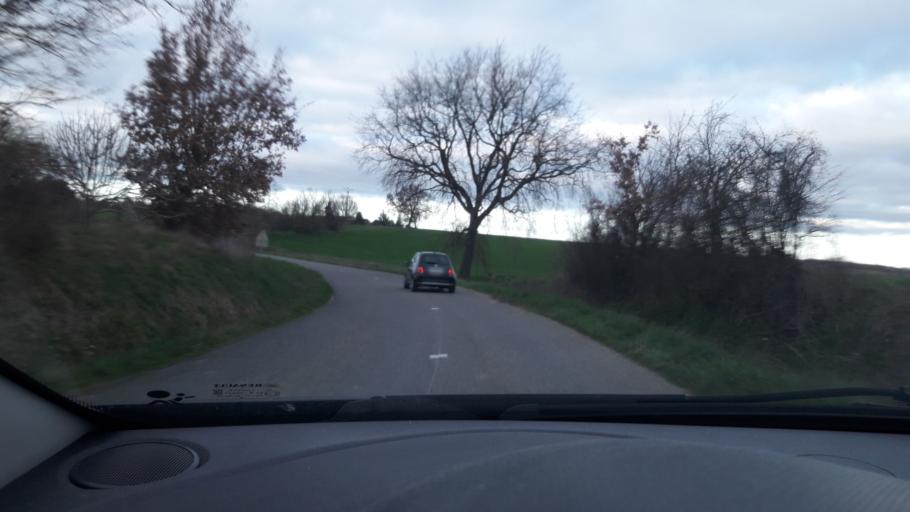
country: FR
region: Midi-Pyrenees
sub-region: Departement du Gers
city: Pujaudran
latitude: 43.6883
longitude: 1.0411
